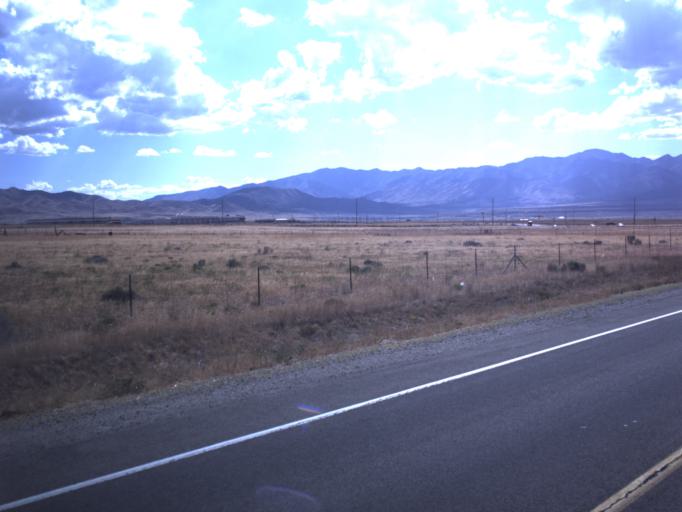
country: US
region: Utah
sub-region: Tooele County
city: Tooele
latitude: 40.5507
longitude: -112.3354
